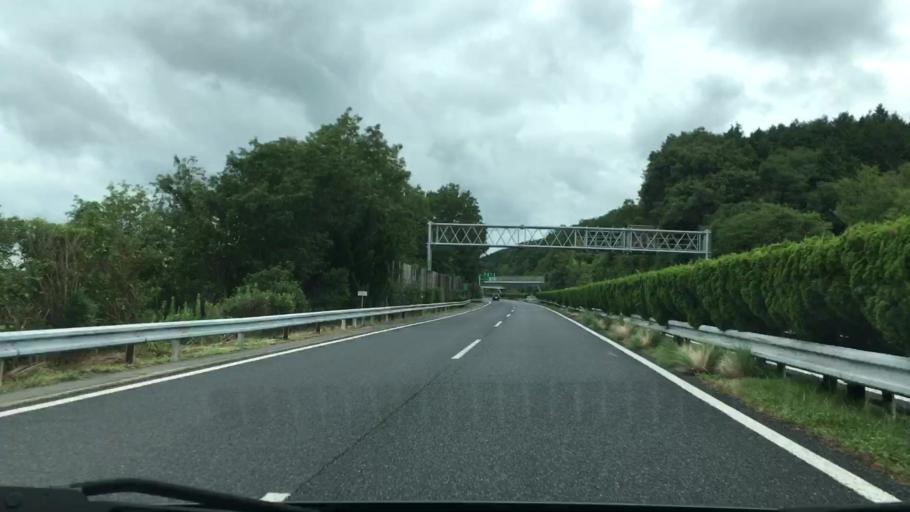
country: JP
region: Okayama
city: Tsuyama
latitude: 35.0386
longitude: 134.1288
